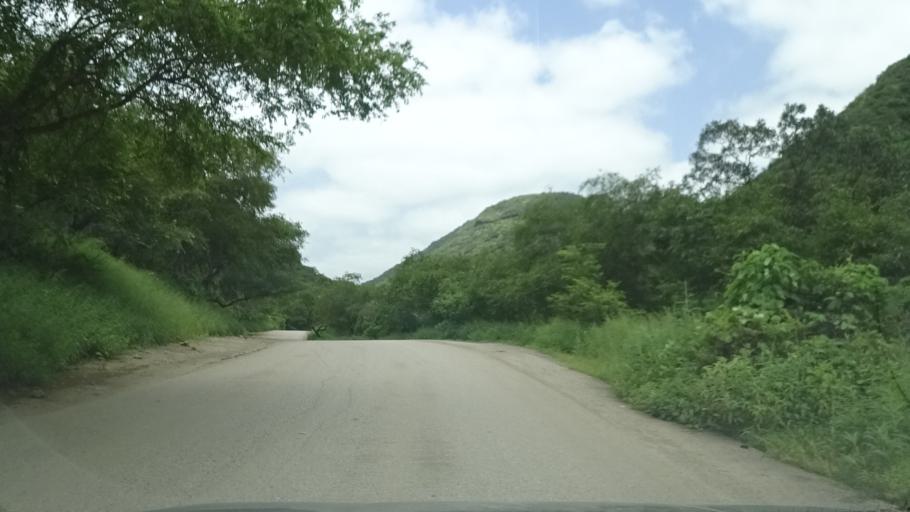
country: OM
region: Zufar
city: Salalah
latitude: 17.1580
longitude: 54.1713
